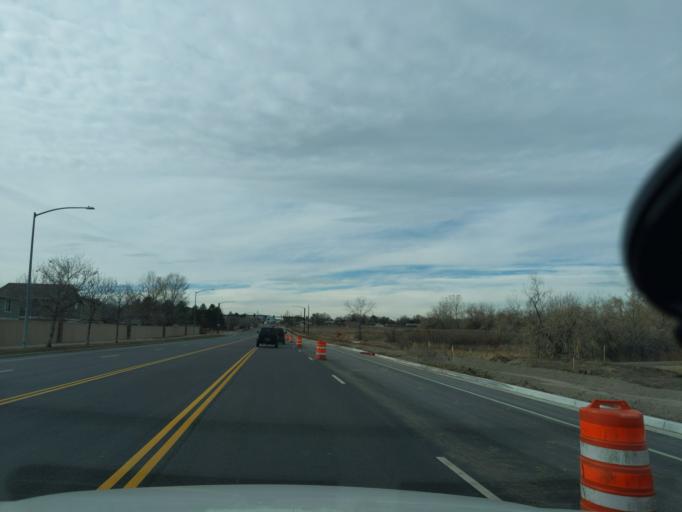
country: US
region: Colorado
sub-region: Adams County
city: Northglenn
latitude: 39.8995
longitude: -104.9542
